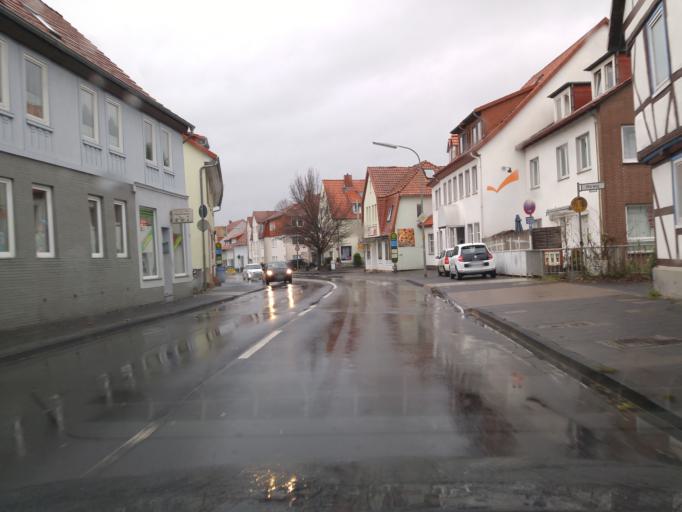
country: DE
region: Lower Saxony
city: Goettingen
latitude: 51.5620
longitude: 9.9321
